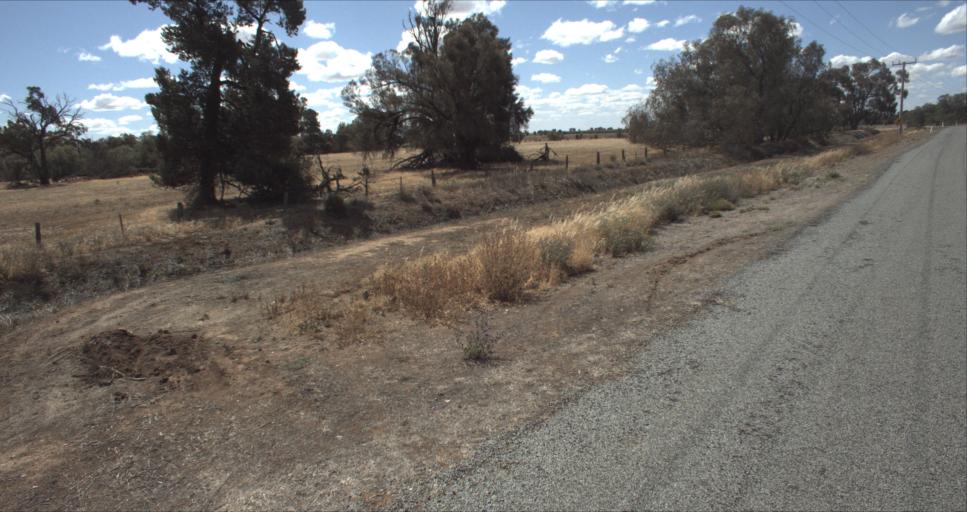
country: AU
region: New South Wales
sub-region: Leeton
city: Leeton
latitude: -34.5200
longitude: 146.2246
